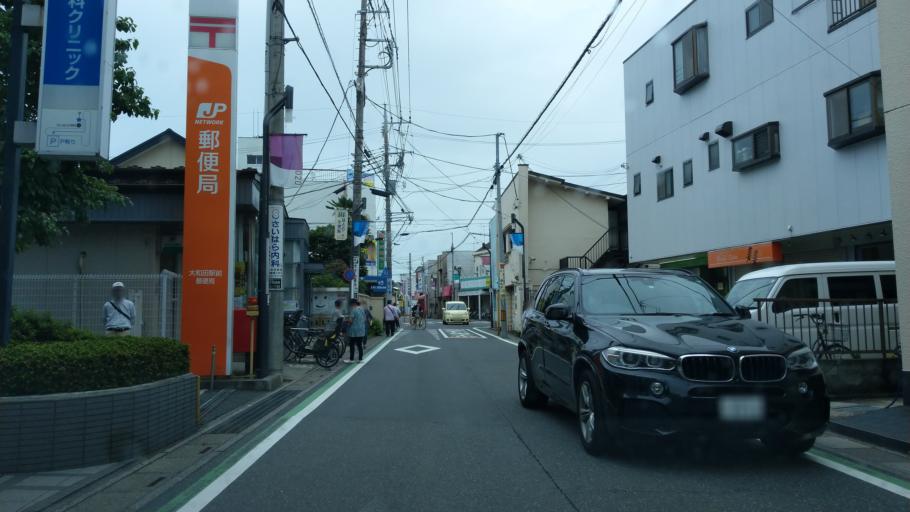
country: JP
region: Saitama
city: Saitama
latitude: 35.9294
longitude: 139.6494
